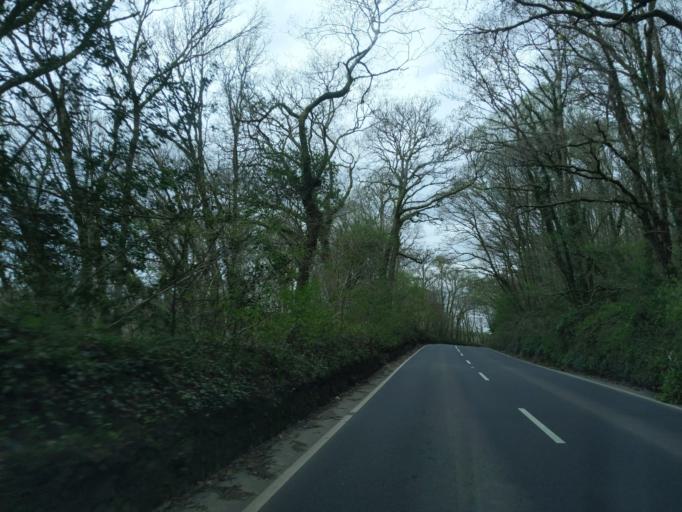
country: GB
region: England
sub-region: Devon
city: Great Torrington
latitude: 50.9340
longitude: -4.1086
